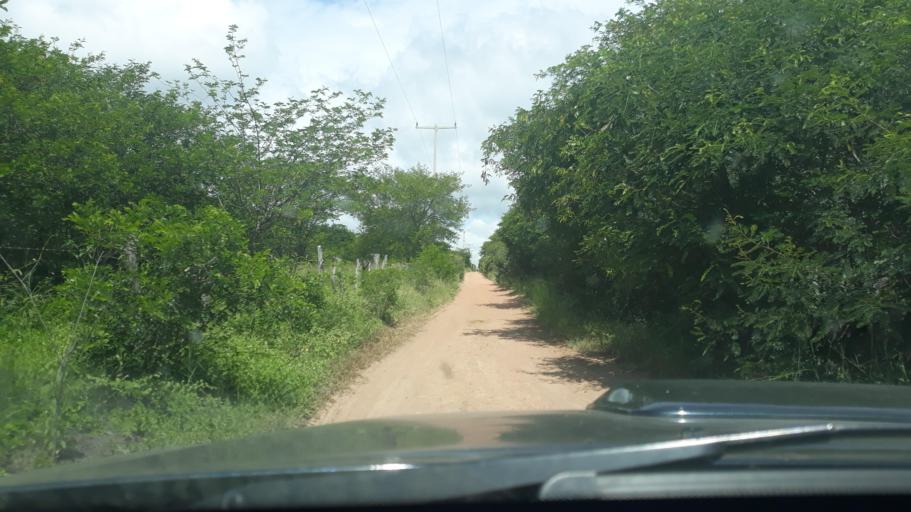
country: BR
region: Bahia
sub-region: Riacho De Santana
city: Riacho de Santana
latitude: -13.8624
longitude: -43.0263
